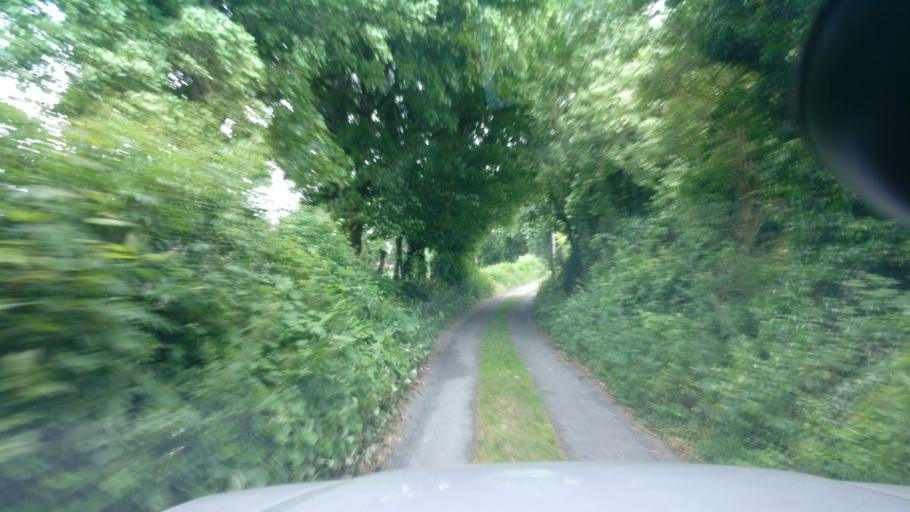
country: IE
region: Connaught
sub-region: County Galway
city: Ballinasloe
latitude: 53.3033
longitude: -8.2870
